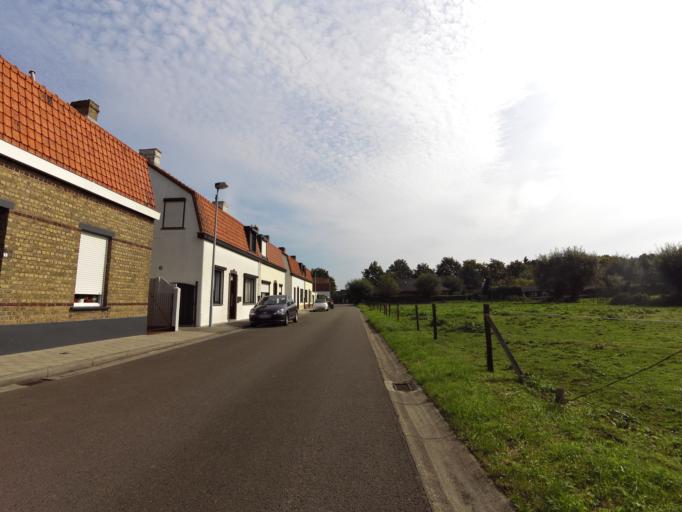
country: BE
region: Flanders
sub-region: Provincie West-Vlaanderen
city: Sint-Kruis
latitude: 51.2184
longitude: 3.2700
